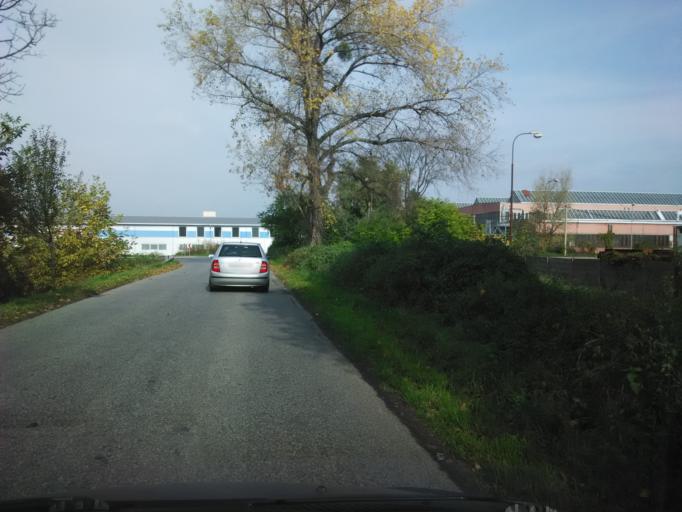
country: SK
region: Nitriansky
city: Komarno
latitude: 47.7620
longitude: 18.0961
